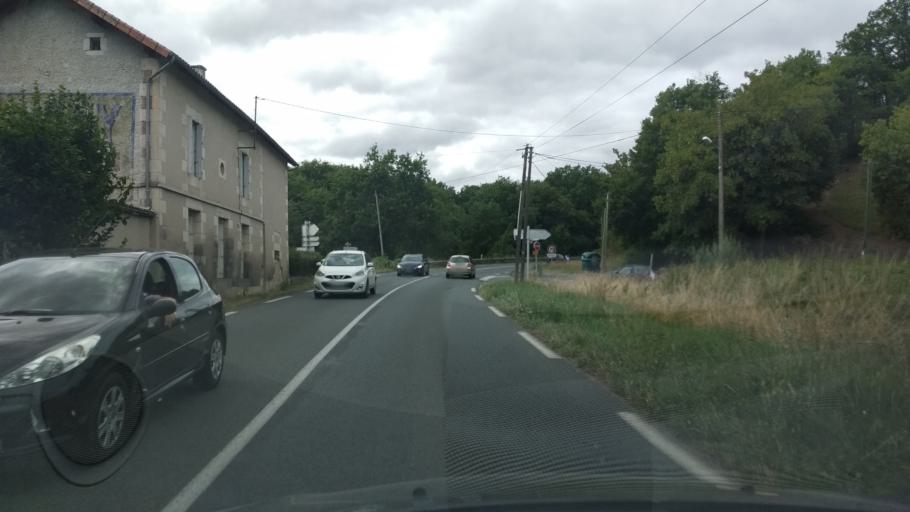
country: FR
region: Poitou-Charentes
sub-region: Departement de la Vienne
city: Saint-Benoit
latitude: 46.5540
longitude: 0.3507
